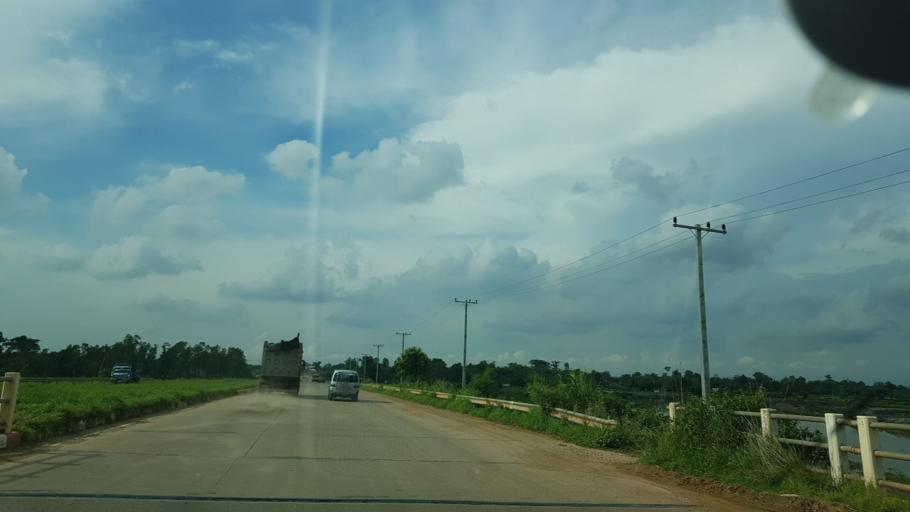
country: TH
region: Nong Khai
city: Nong Khai
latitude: 17.9669
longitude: 102.7211
